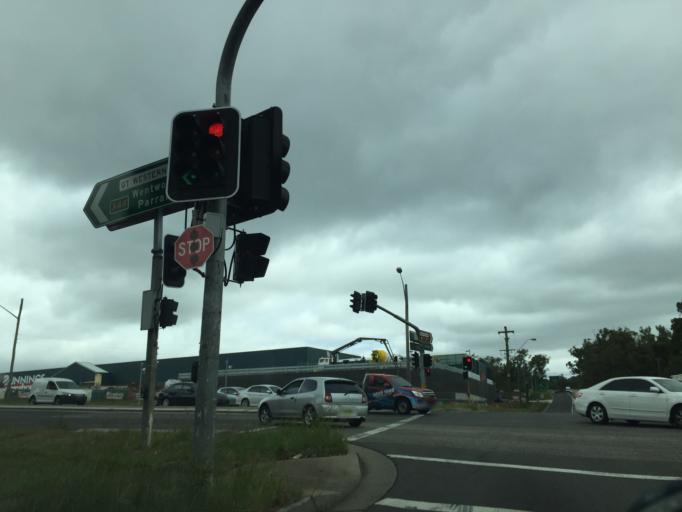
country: AU
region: New South Wales
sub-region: Blacktown
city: Blacktown
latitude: -33.7978
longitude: 150.8971
